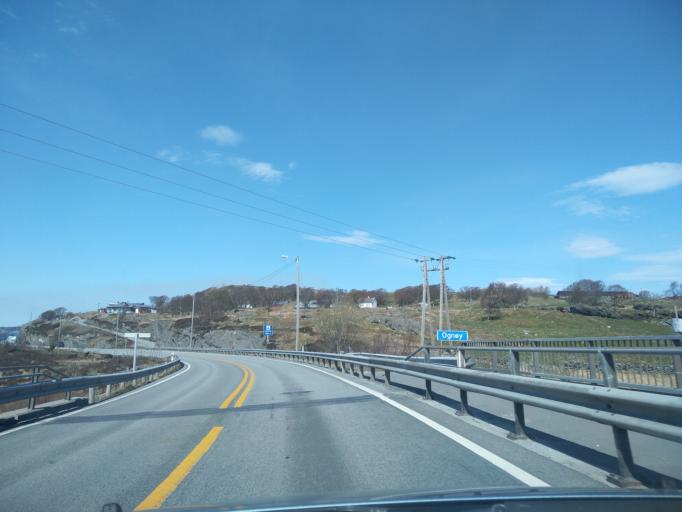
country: NO
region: Rogaland
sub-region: Bokn
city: Bokn
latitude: 59.2533
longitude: 5.4723
